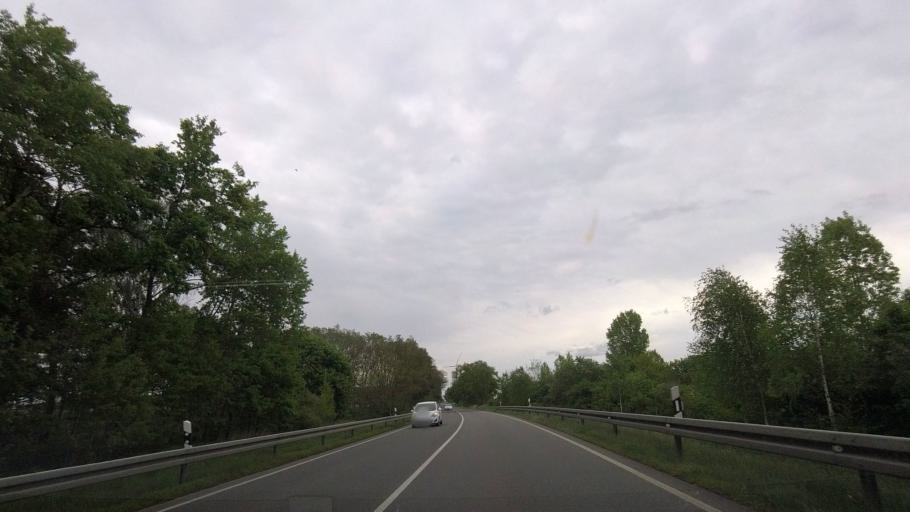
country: DE
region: Brandenburg
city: Luckau
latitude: 51.8690
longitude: 13.7535
